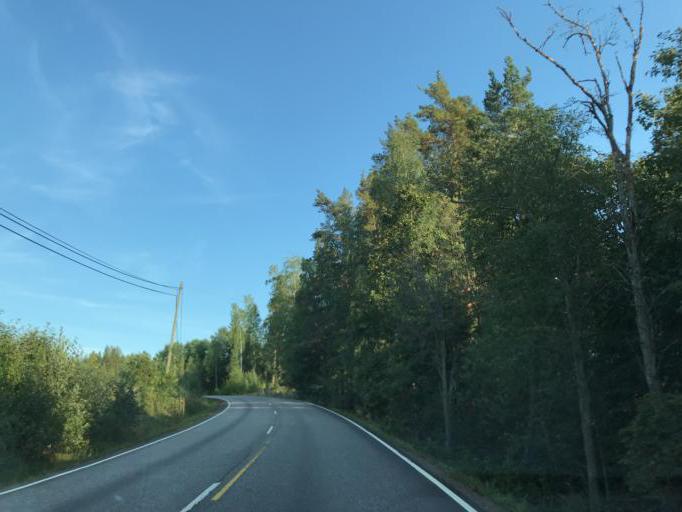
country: FI
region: Uusimaa
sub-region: Helsinki
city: Vihti
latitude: 60.4197
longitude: 24.3693
